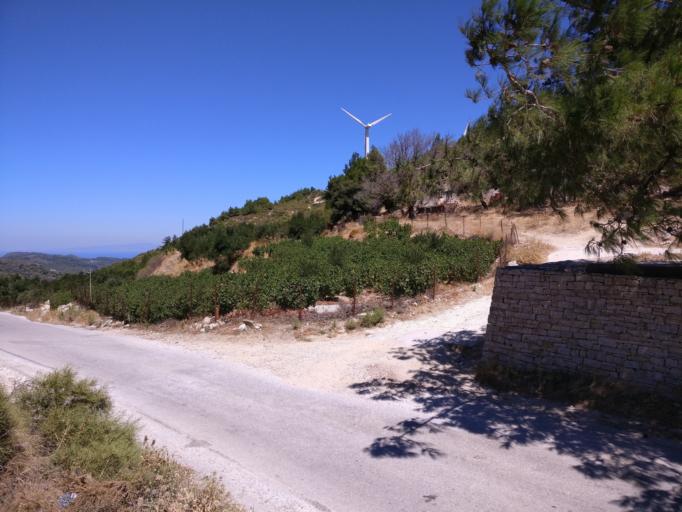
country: GR
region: North Aegean
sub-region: Nomos Samou
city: Marathokampos
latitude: 37.7344
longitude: 26.7035
